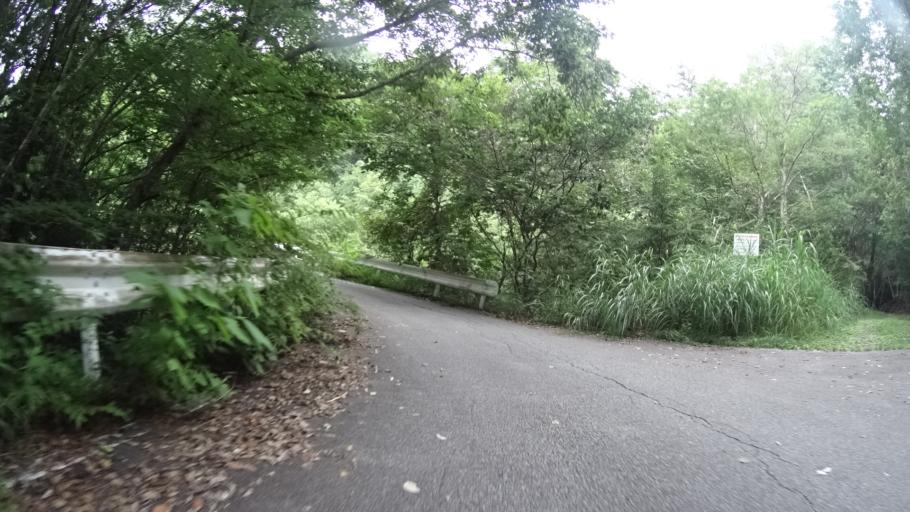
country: JP
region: Yamanashi
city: Kofu-shi
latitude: 35.8048
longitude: 138.5981
